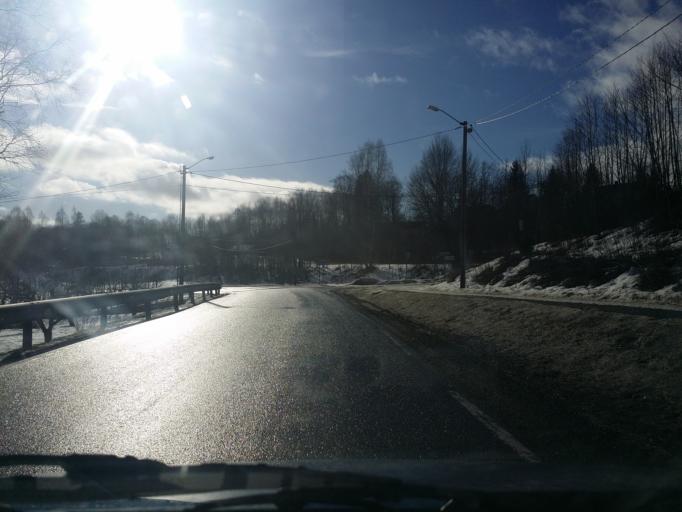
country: NO
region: Buskerud
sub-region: Lier
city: Lierbyen
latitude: 59.8084
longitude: 10.2211
